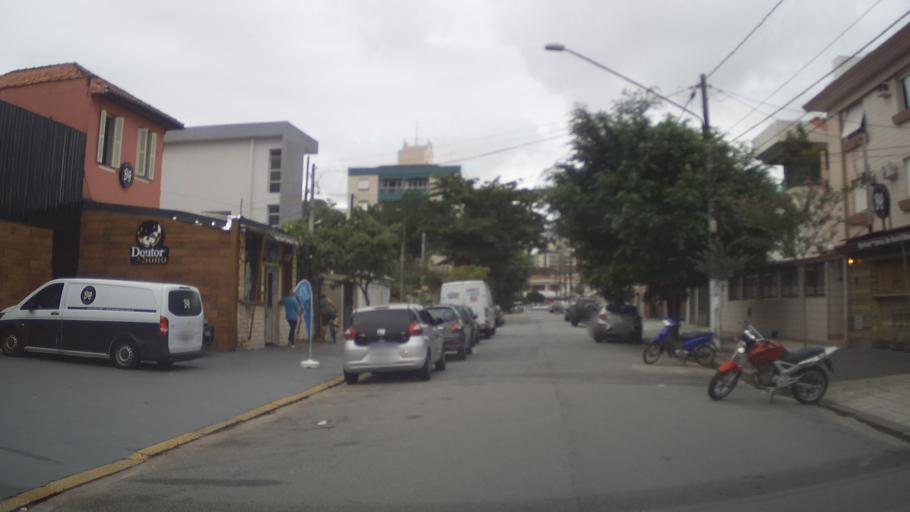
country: BR
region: Sao Paulo
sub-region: Santos
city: Santos
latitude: -23.9591
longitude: -46.3201
